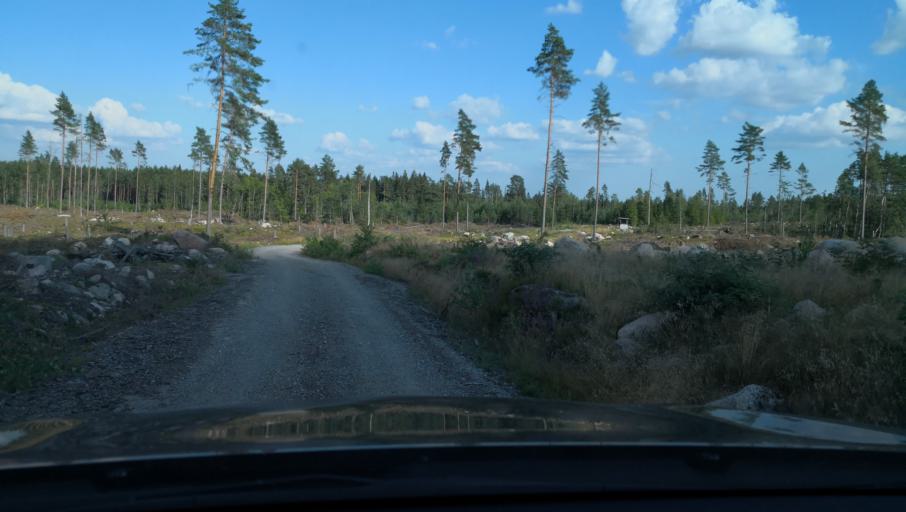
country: SE
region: Vaestmanland
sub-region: Vasteras
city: Skultuna
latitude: 59.7084
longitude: 16.3846
